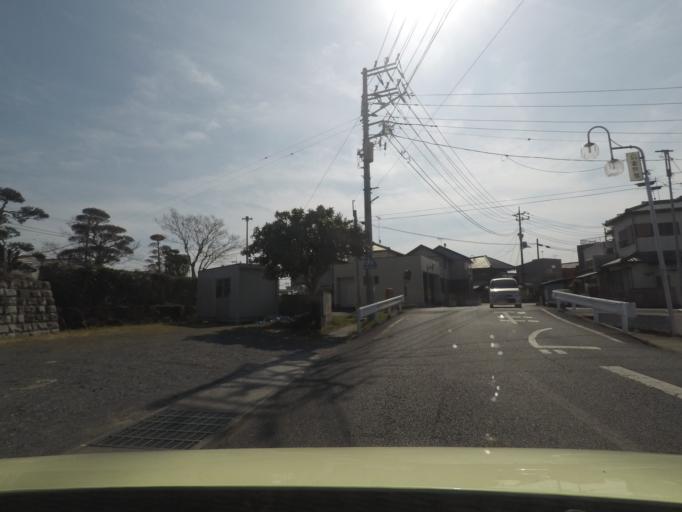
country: JP
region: Ibaraki
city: Ishioka
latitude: 36.1709
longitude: 140.3533
